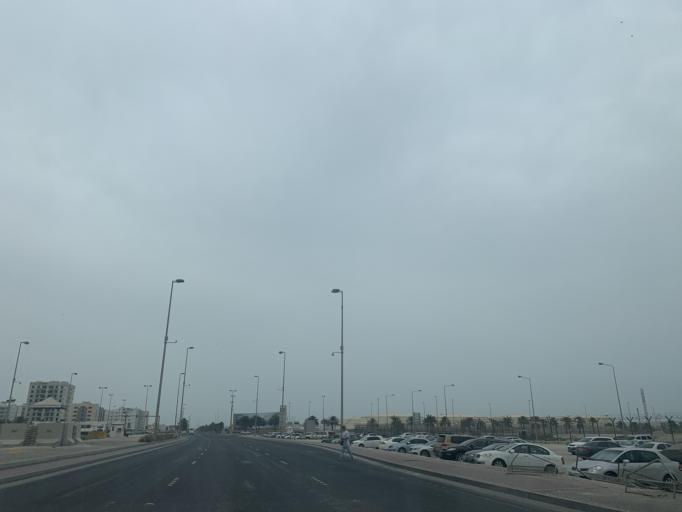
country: BH
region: Muharraq
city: Al Hadd
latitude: 26.2227
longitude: 50.6577
